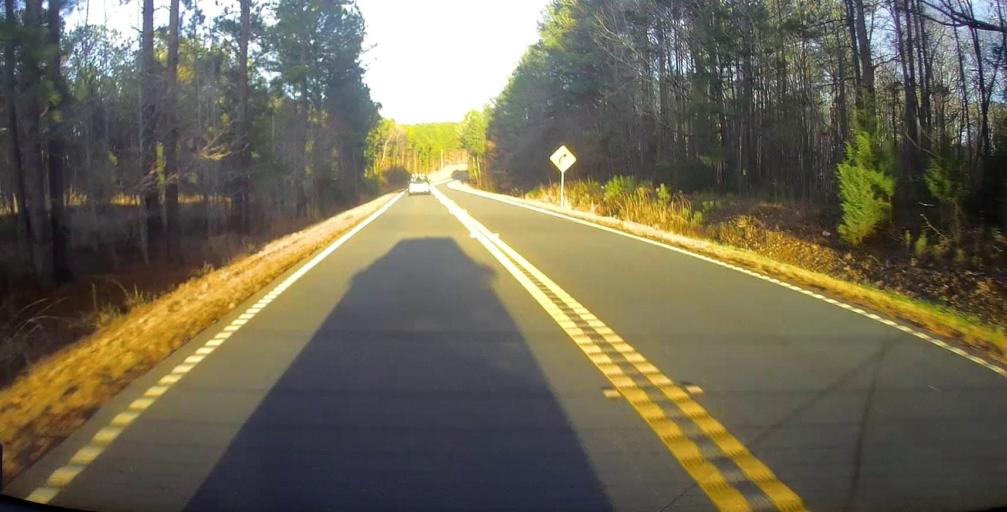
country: US
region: Georgia
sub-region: Talbot County
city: Sardis
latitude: 32.7246
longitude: -84.6368
